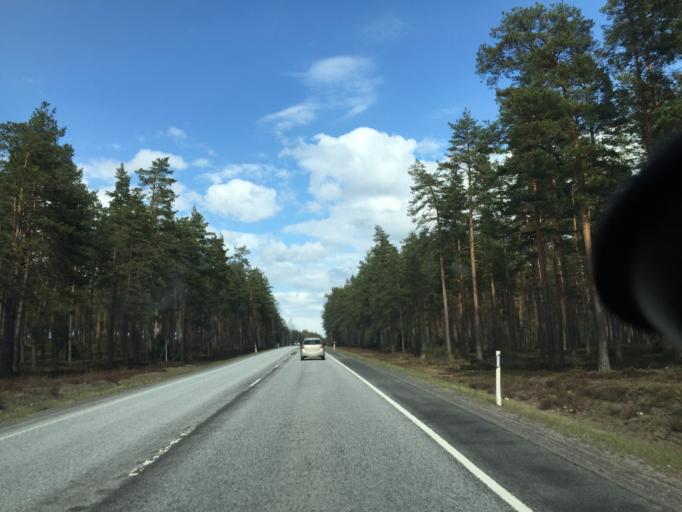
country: FI
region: Uusimaa
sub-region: Raaseporin
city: Pohja
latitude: 60.0211
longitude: 23.5737
